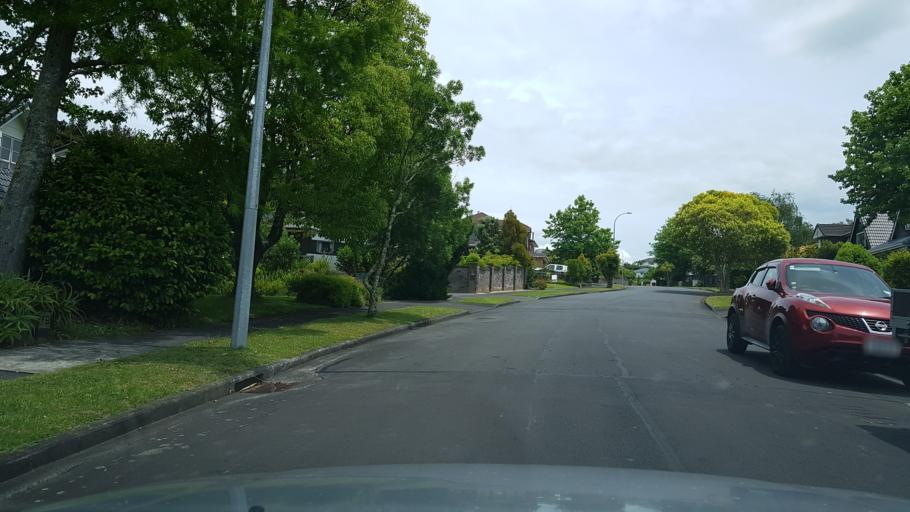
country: NZ
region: Auckland
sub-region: Auckland
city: North Shore
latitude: -36.8203
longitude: 174.7142
